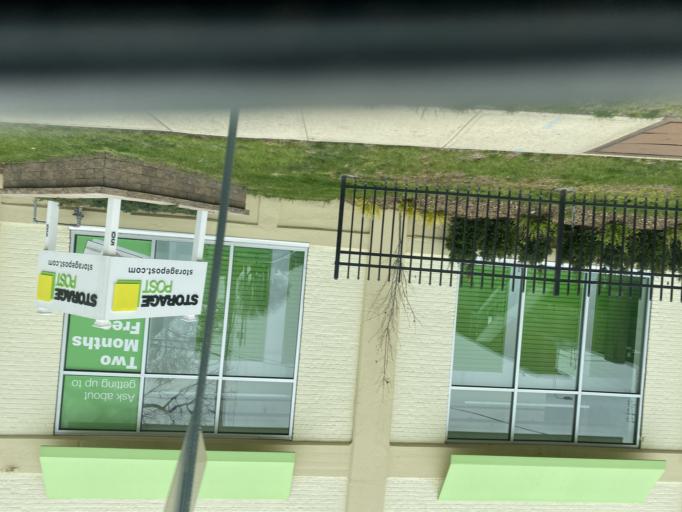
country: US
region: New York
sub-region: Nassau County
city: Floral Park
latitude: 40.7247
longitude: -73.7080
